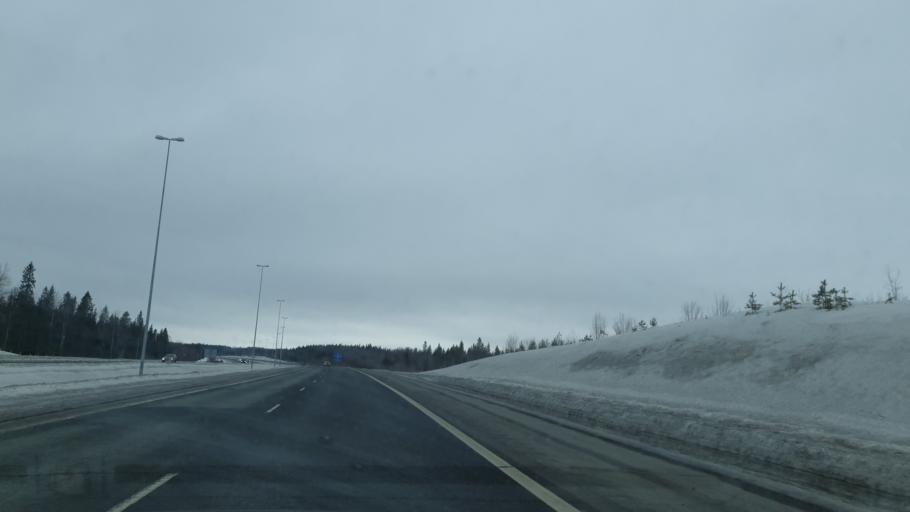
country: FI
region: Lapland
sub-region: Kemi-Tornio
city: Keminmaa
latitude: 65.8234
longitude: 24.4718
